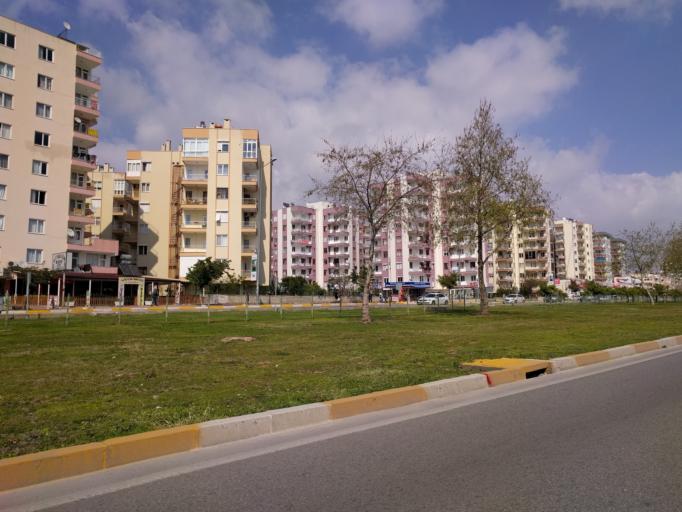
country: TR
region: Antalya
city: Antalya
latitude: 36.9002
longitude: 30.6555
